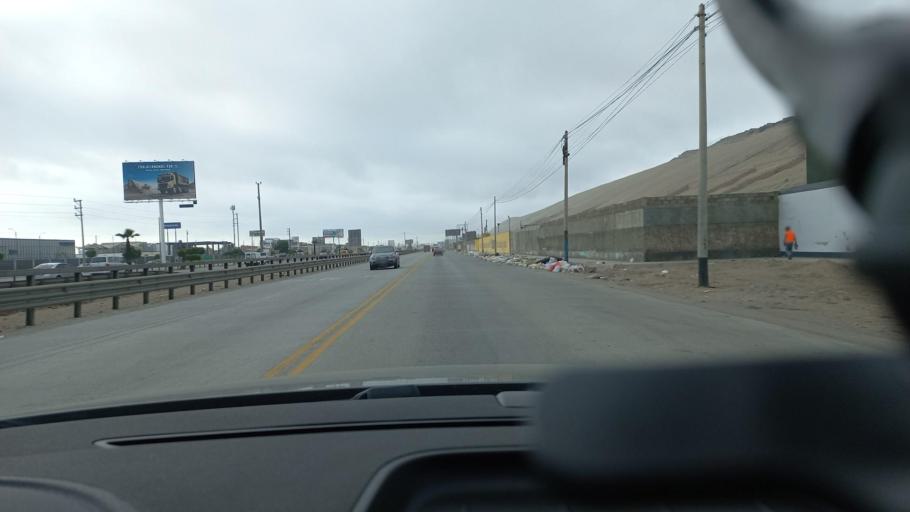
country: PE
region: Lima
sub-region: Lima
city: Surco
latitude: -12.2461
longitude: -76.9363
